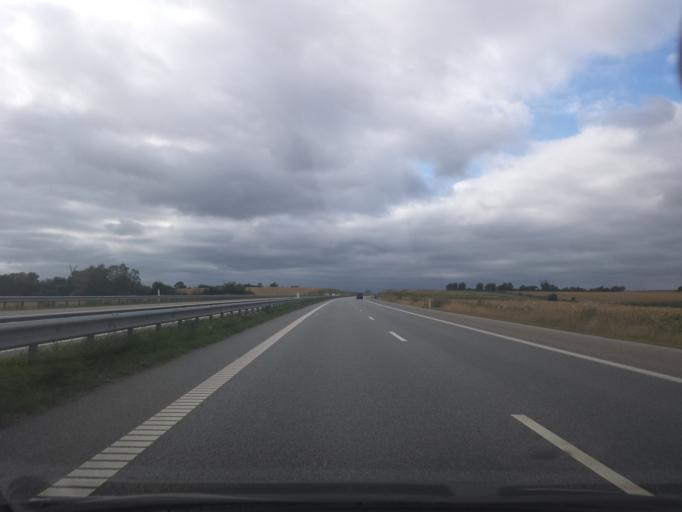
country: DK
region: South Denmark
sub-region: Sonderborg Kommune
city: Broager
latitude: 54.9371
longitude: 9.6779
